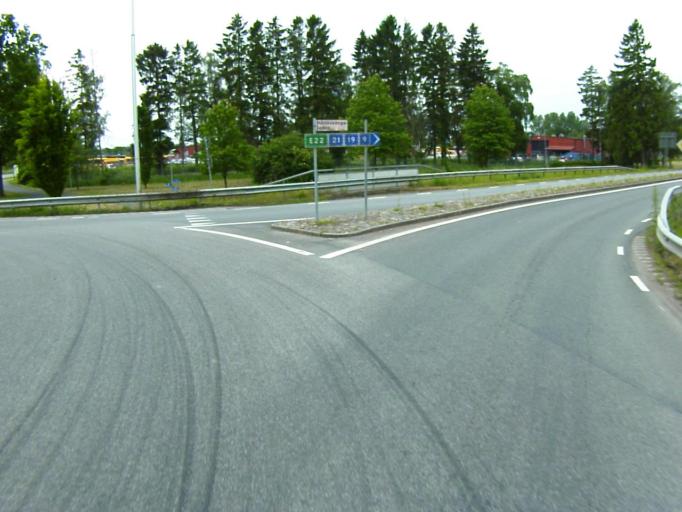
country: SE
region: Skane
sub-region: Kristianstads Kommun
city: Kristianstad
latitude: 56.0429
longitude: 14.1513
